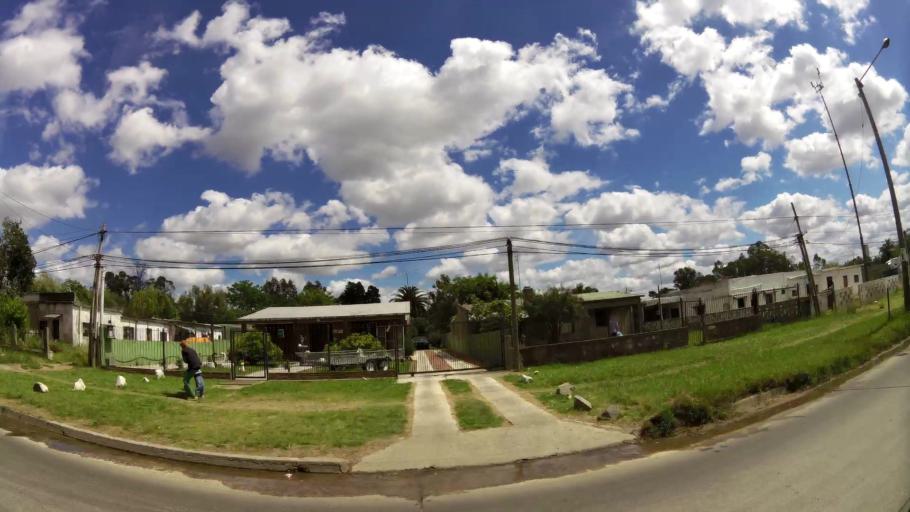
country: UY
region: Canelones
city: Colonia Nicolich
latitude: -34.8245
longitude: -56.1121
